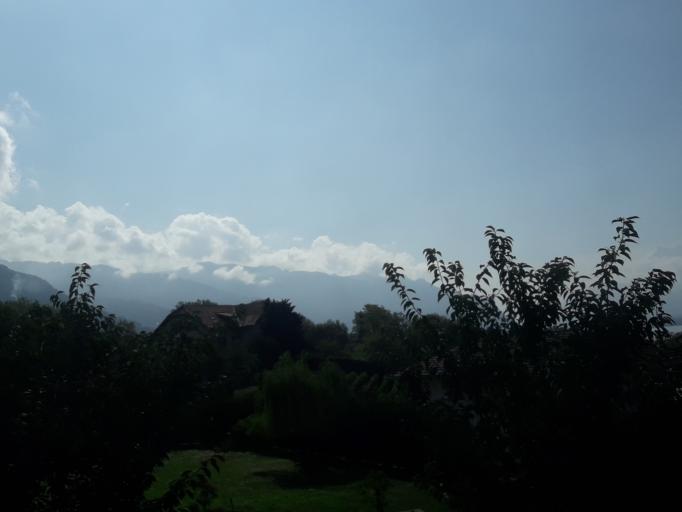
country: CH
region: Vaud
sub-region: Riviera-Pays-d'Enhaut District
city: Blonay
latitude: 46.4704
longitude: 6.8755
